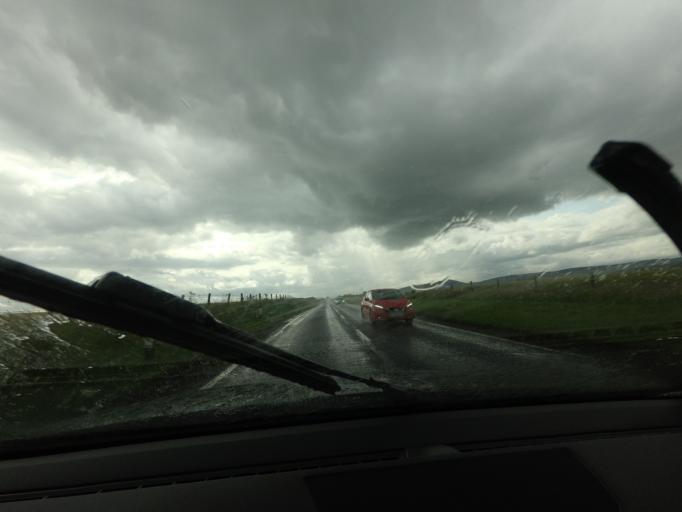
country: GB
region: Scotland
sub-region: Highland
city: Fortrose
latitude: 57.5019
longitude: -4.1287
